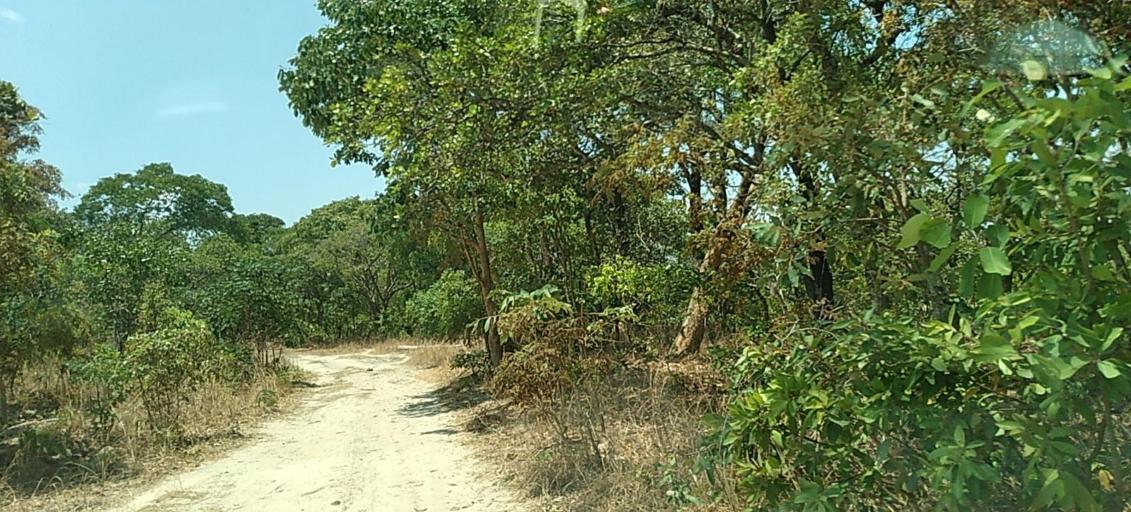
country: ZM
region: Central
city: Kapiri Mposhi
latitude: -13.6672
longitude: 28.4918
